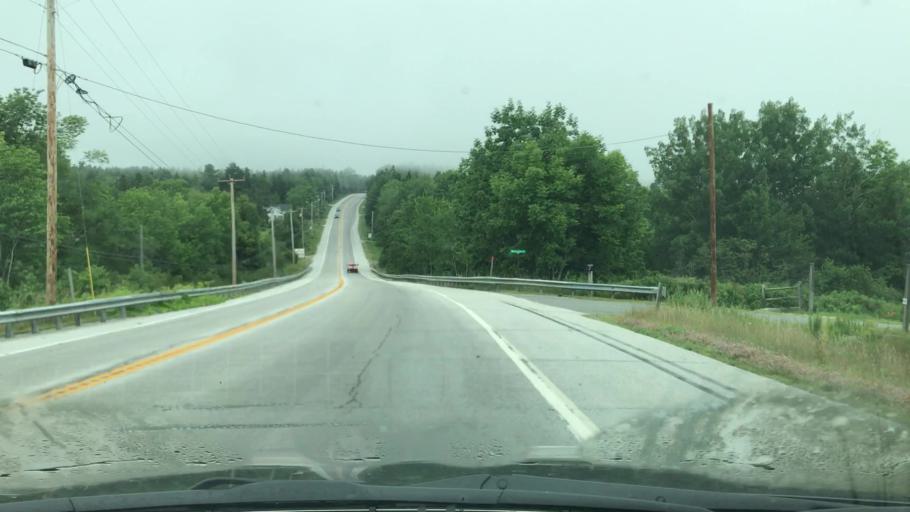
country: US
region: Maine
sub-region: Waldo County
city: Northport
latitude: 44.3044
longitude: -68.9775
